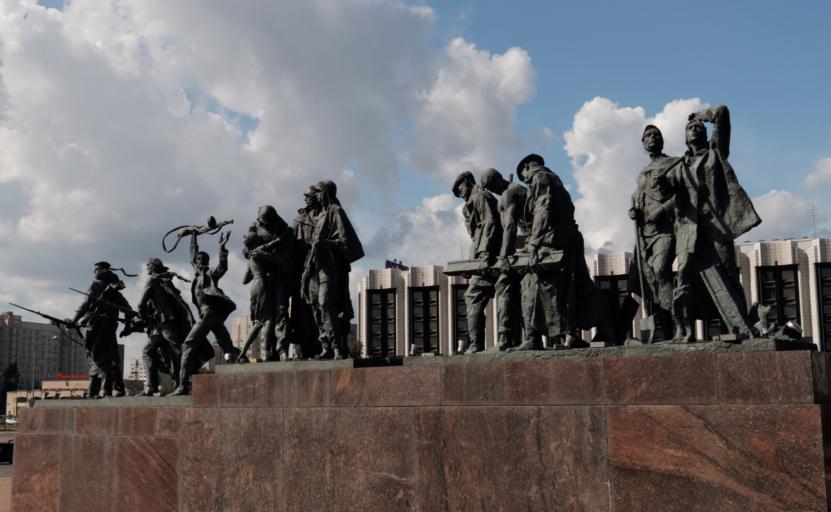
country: RU
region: St.-Petersburg
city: Kupchino
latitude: 59.8428
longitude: 30.3218
